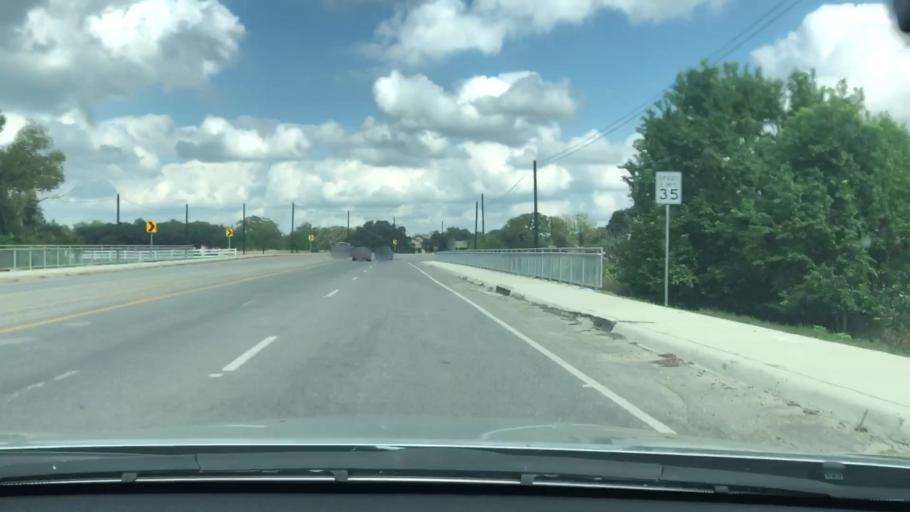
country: US
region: Texas
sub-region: Kendall County
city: Boerne
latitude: 29.7884
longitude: -98.7134
